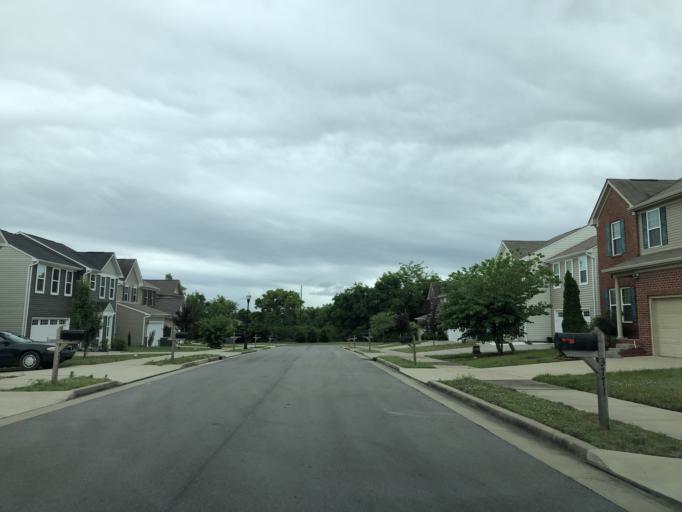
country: US
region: Tennessee
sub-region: Davidson County
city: Nashville
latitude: 36.2564
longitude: -86.7760
